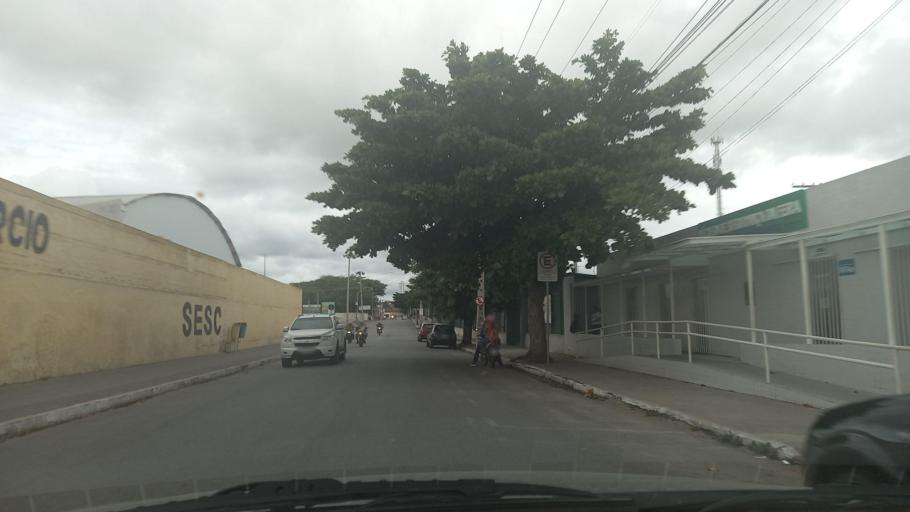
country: BR
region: Pernambuco
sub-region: Caruaru
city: Caruaru
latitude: -8.2930
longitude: -35.9720
